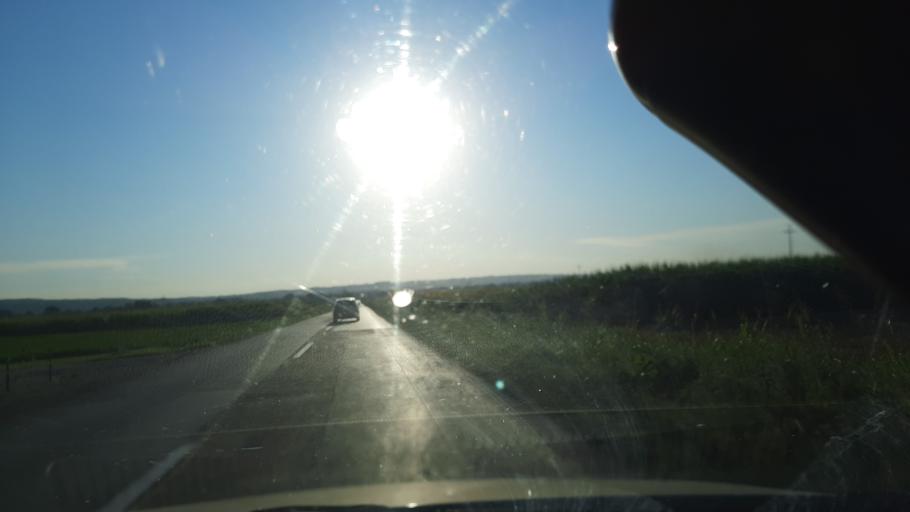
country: RS
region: Central Serbia
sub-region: Branicevski Okrug
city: Malo Crnice
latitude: 44.5851
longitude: 21.2922
